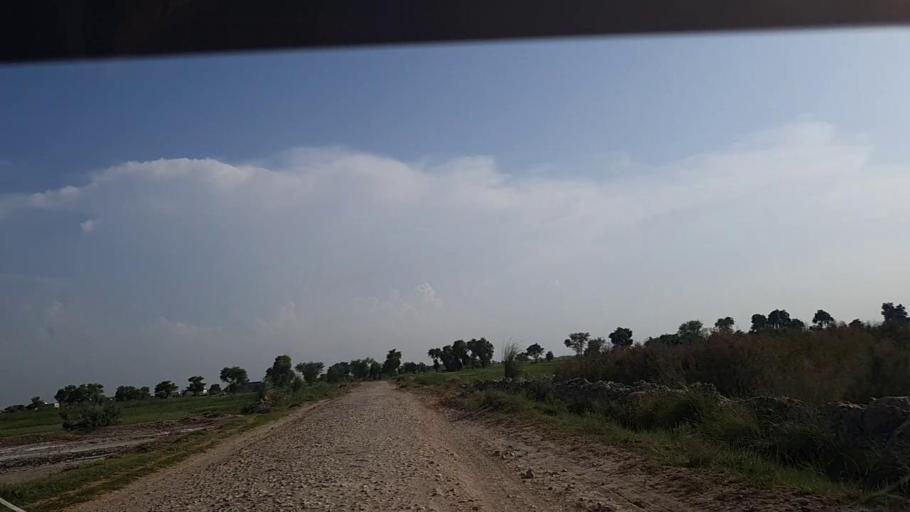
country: PK
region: Sindh
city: Khanpur
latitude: 27.8442
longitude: 69.3760
